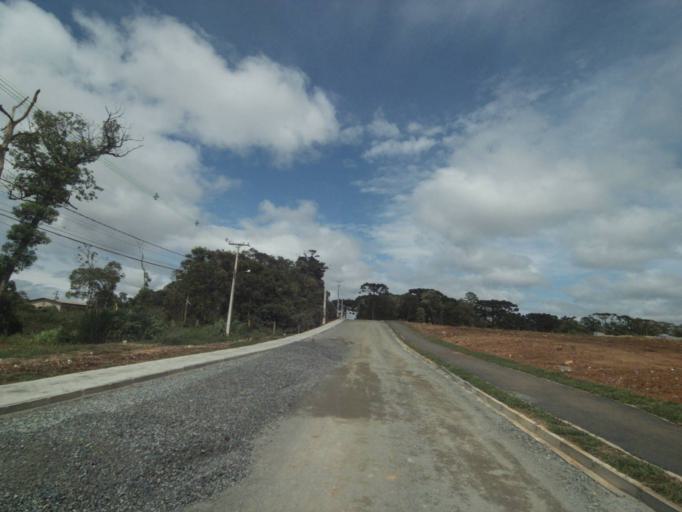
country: BR
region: Parana
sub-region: Campina Grande Do Sul
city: Campina Grande do Sul
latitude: -25.3335
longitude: -49.0692
